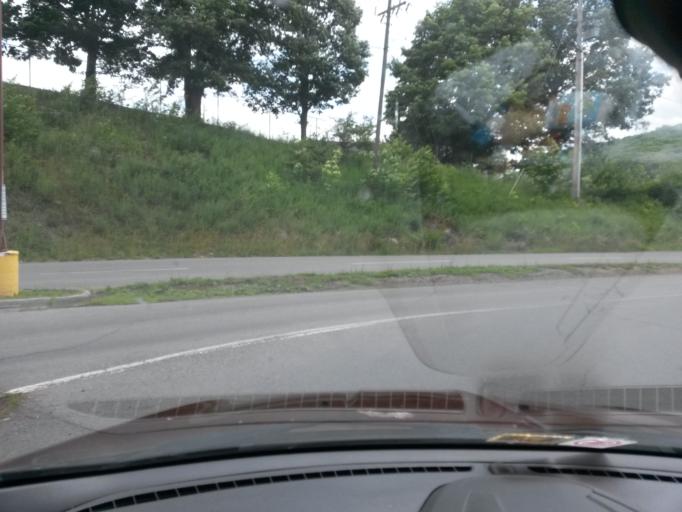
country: US
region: West Virginia
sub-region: Mercer County
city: Bluefield
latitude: 37.2990
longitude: -81.1666
